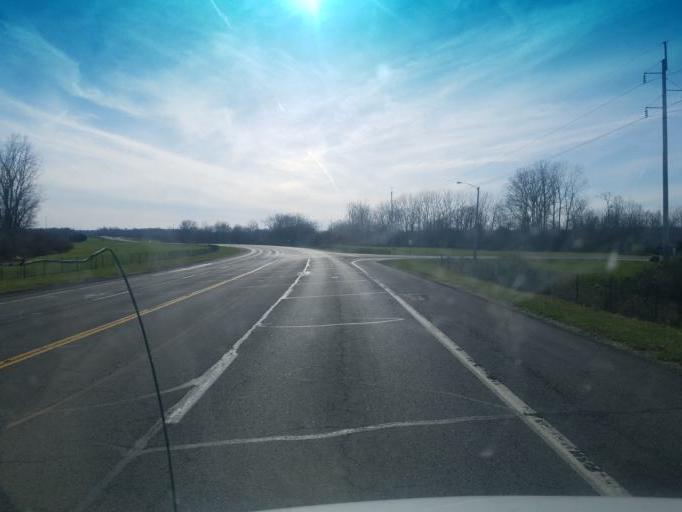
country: US
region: Ohio
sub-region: Champaign County
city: North Lewisburg
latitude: 40.3296
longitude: -83.5731
